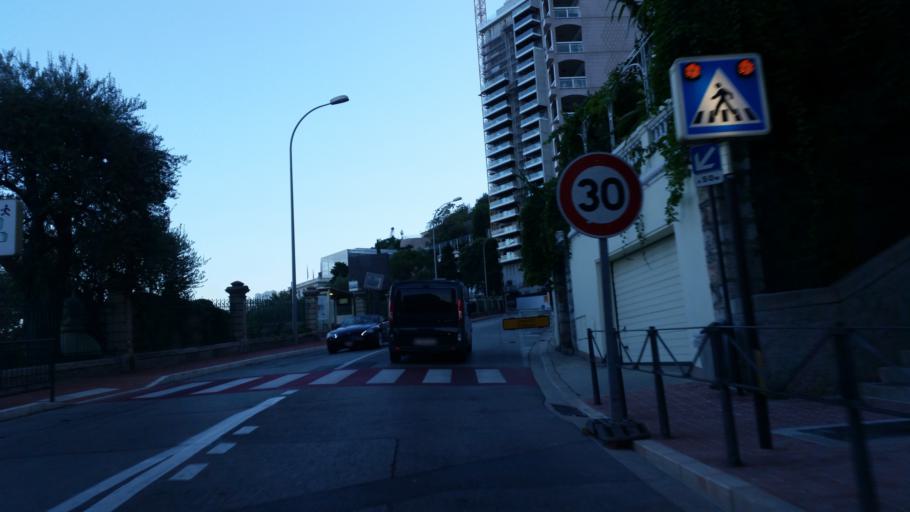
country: MC
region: Commune de Monaco
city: Monaco
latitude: 43.7343
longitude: 7.4149
